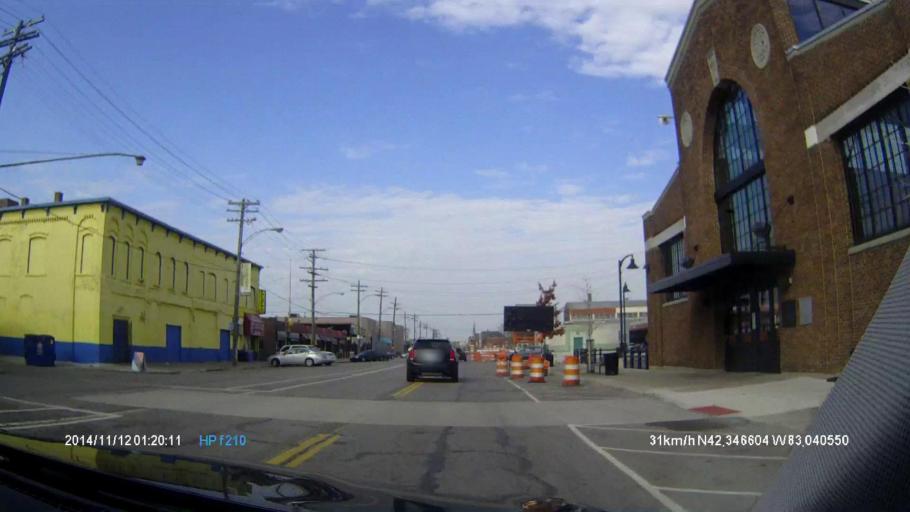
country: US
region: Michigan
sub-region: Wayne County
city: Detroit
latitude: 42.3468
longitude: -83.0407
